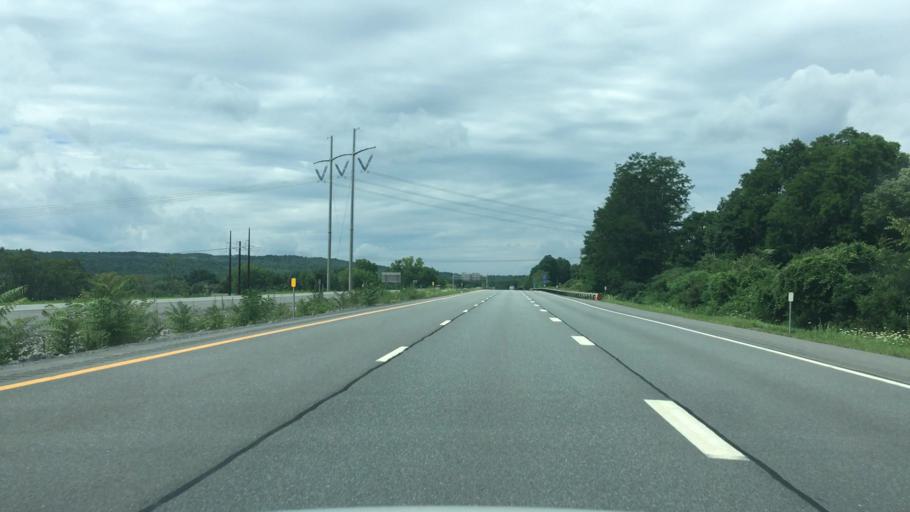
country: US
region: New York
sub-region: Schenectady County
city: Rotterdam
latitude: 42.7815
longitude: -74.0358
